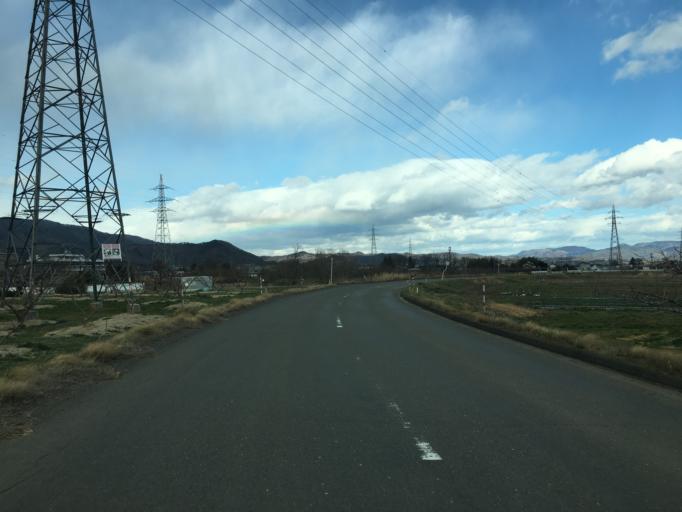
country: JP
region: Fukushima
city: Hobaramachi
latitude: 37.8681
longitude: 140.5388
